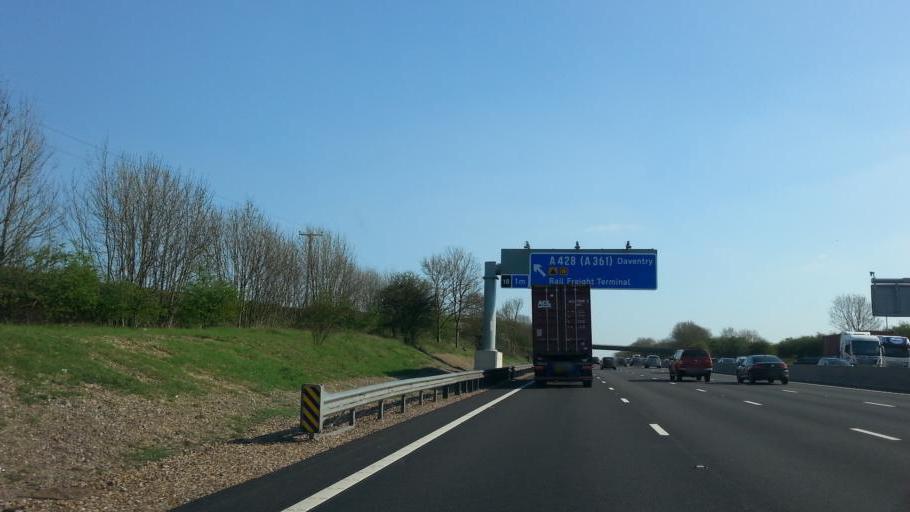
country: GB
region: England
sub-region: Leicestershire
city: Lutterworth
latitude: 52.3710
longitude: -1.1615
